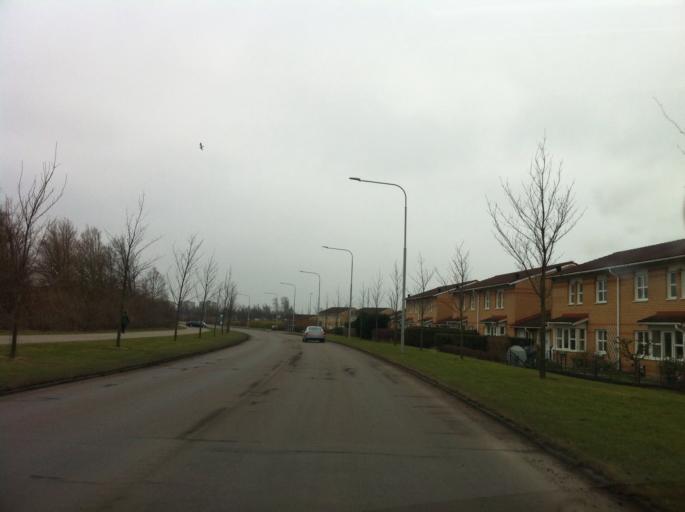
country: SE
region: Skane
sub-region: Landskrona
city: Landskrona
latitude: 55.8908
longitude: 12.8165
